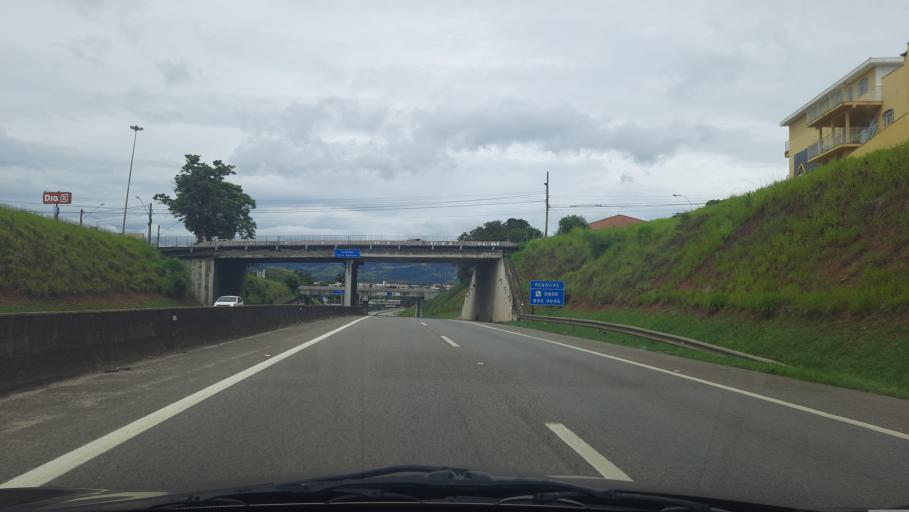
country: BR
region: Sao Paulo
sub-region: Sao Joao Da Boa Vista
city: Sao Joao da Boa Vista
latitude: -21.9867
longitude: -46.7894
